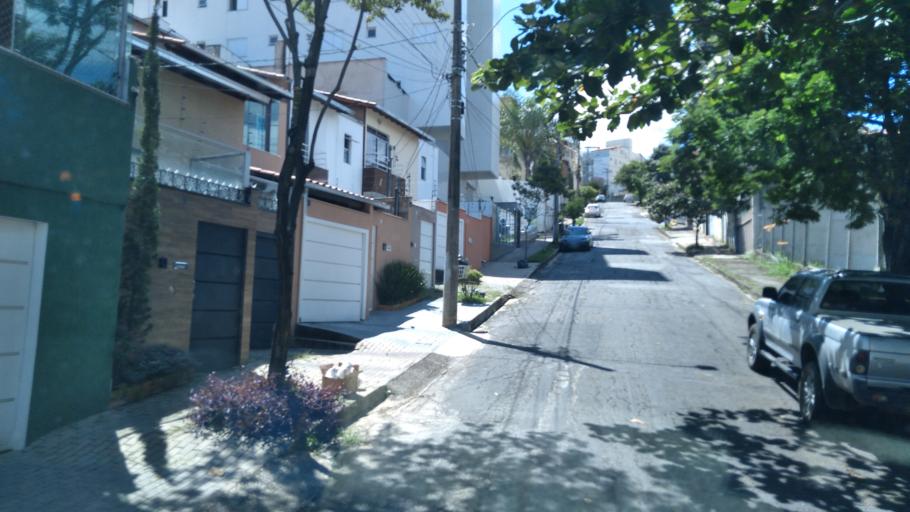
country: BR
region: Minas Gerais
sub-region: Belo Horizonte
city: Belo Horizonte
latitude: -19.8720
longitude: -43.9193
